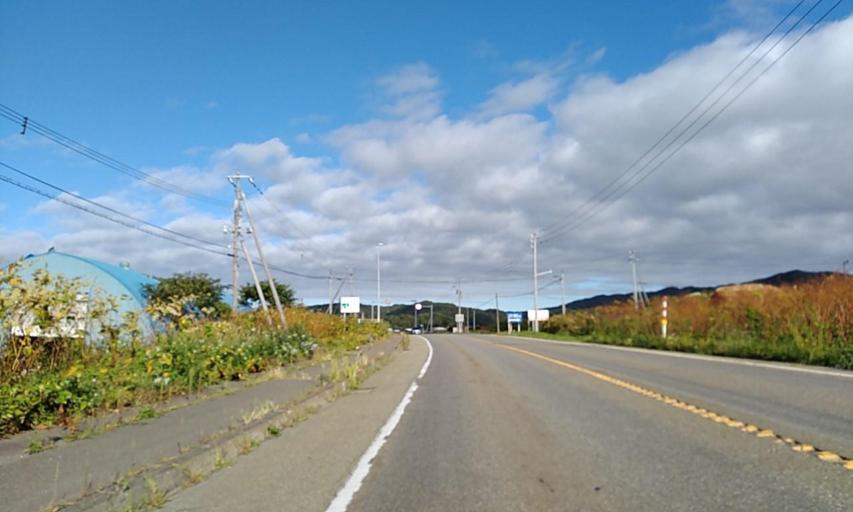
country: JP
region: Hokkaido
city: Shizunai-furukawacho
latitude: 42.2424
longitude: 142.5880
